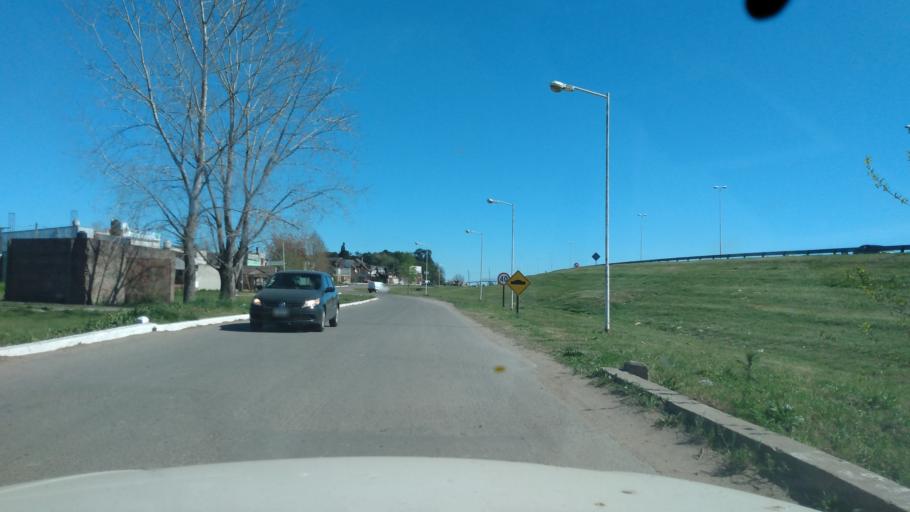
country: AR
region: Buenos Aires
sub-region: Partido de Lujan
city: Lujan
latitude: -34.5628
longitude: -59.0870
